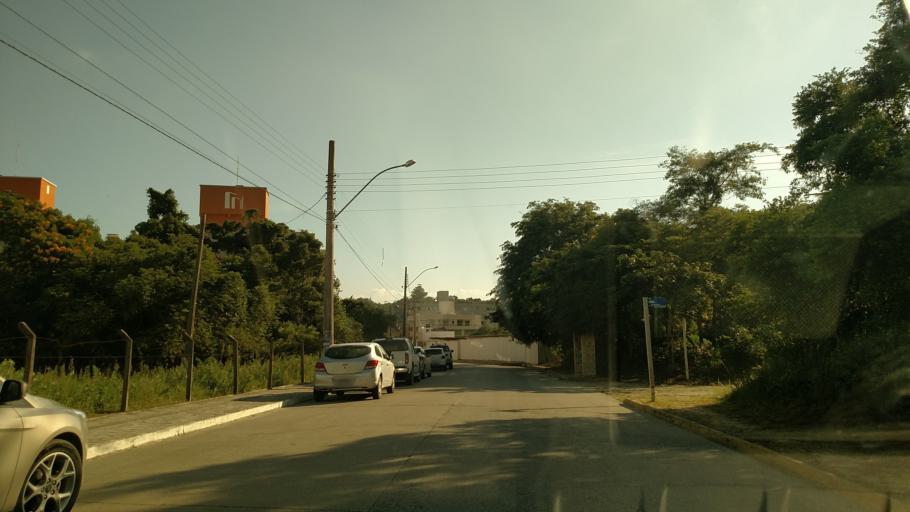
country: BR
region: Santa Catarina
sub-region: Porto Belo
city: Porto Belo
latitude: -27.1536
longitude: -48.5020
